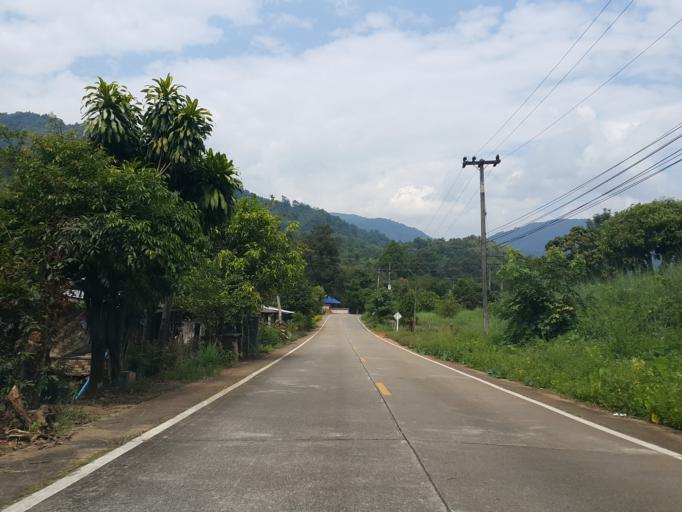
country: TH
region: Mae Hong Son
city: Mae Hong Son
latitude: 19.4578
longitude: 97.9670
